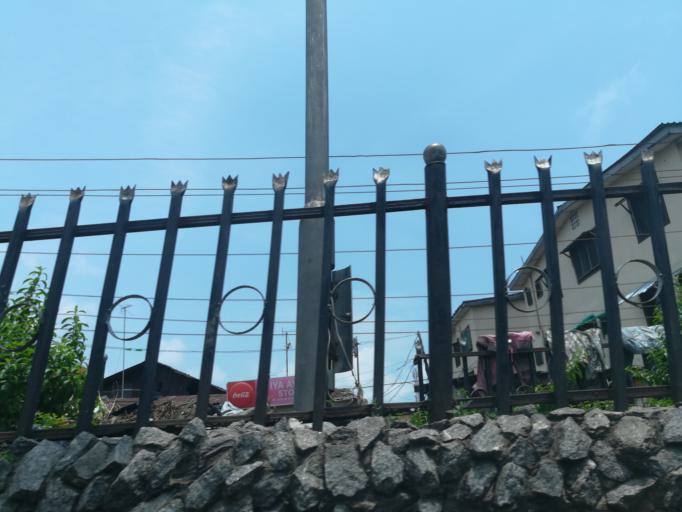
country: NG
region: Lagos
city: Lagos
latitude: 6.4541
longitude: 3.3984
